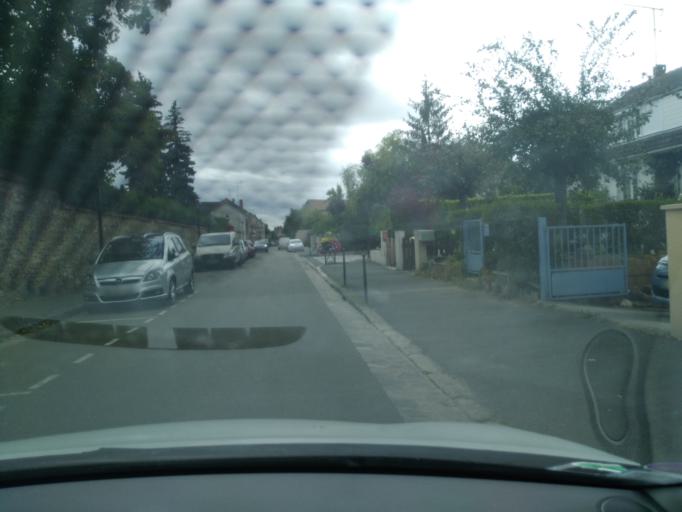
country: FR
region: Ile-de-France
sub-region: Departement des Yvelines
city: Crespieres
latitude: 48.8858
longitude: 1.9231
